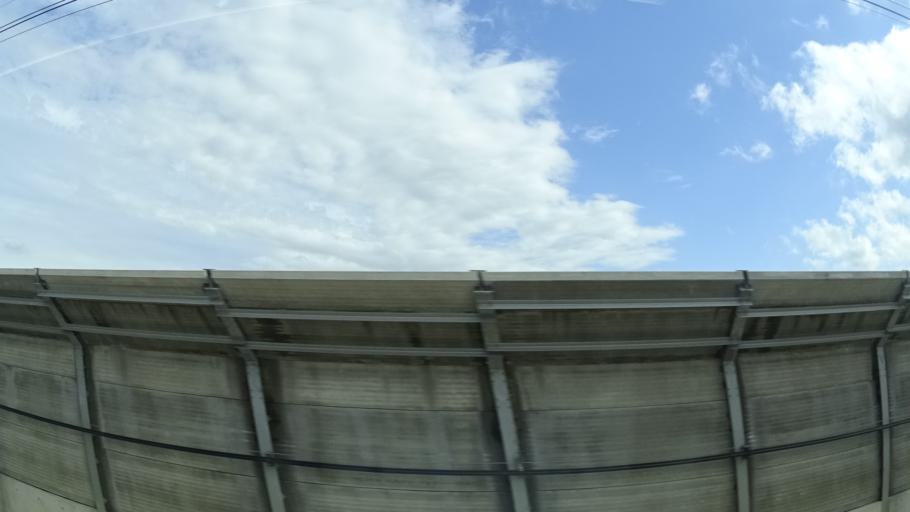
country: JP
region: Toyama
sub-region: Oyabe Shi
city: Oyabe
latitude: 36.6696
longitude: 136.8851
